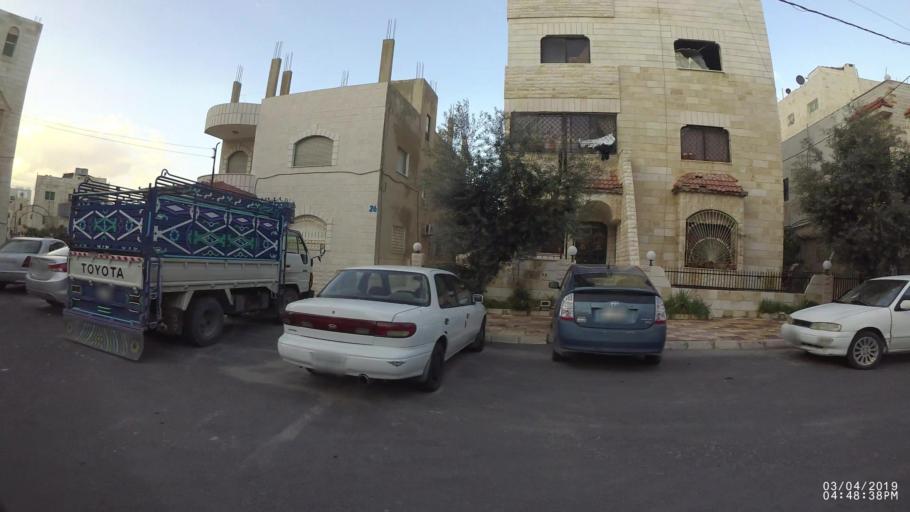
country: JO
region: Amman
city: Al Bunayyat ash Shamaliyah
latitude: 31.9151
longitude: 35.8914
